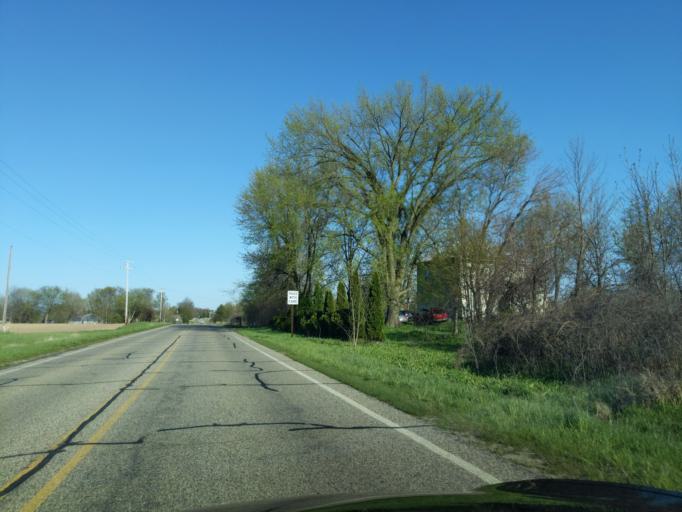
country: US
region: Michigan
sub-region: Ionia County
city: Portland
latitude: 42.8817
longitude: -84.9836
